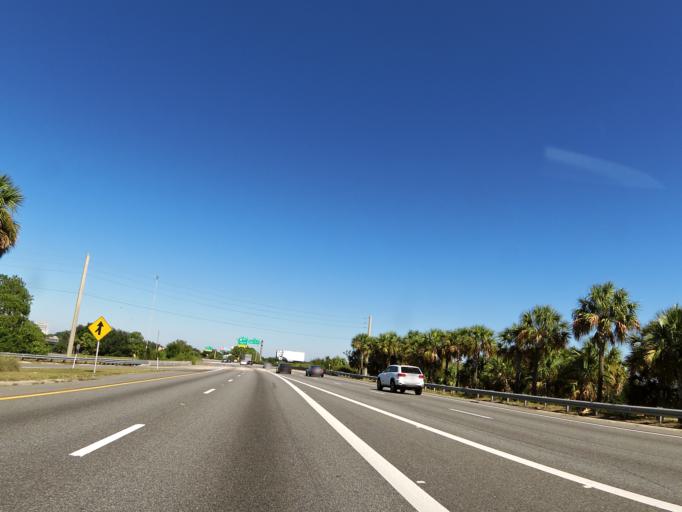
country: US
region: Florida
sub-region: Duval County
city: Jacksonville
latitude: 30.3322
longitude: -81.6717
